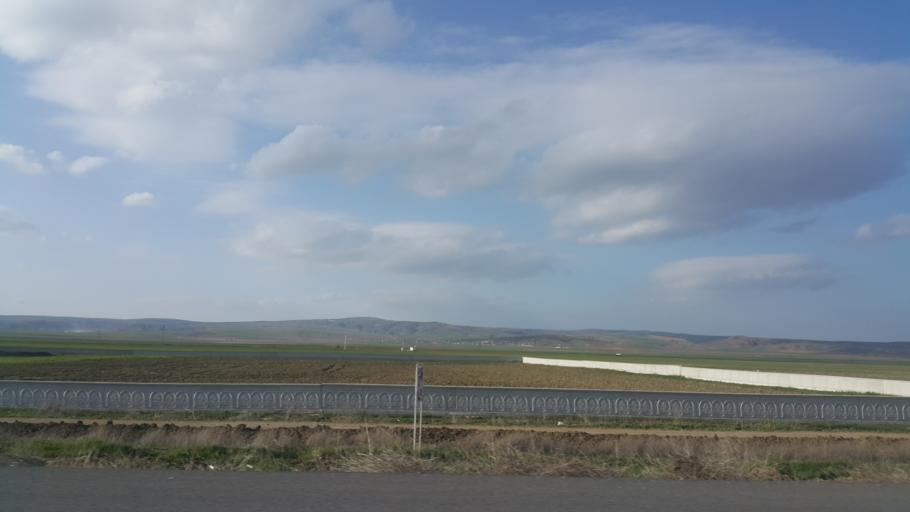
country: TR
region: Konya
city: Kulu
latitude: 39.1527
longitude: 33.2550
